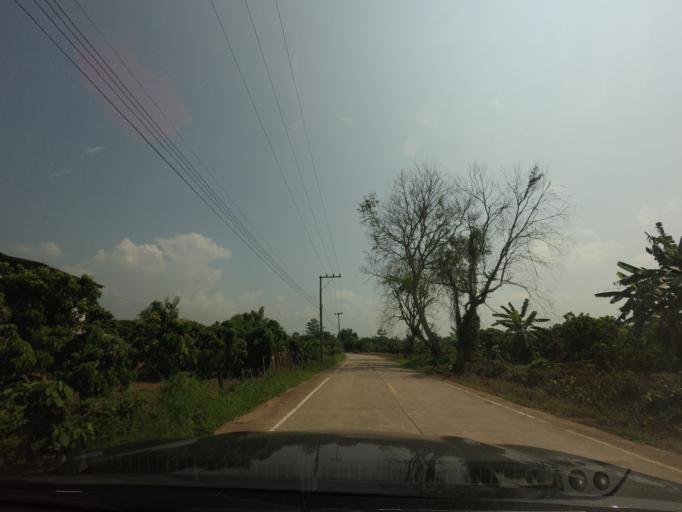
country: TH
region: Nan
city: Nan
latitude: 18.8597
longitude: 100.8091
